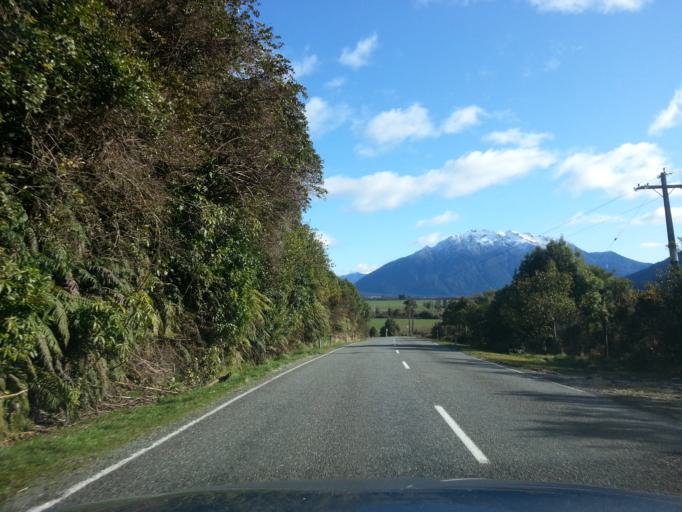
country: NZ
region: West Coast
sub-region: Grey District
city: Greymouth
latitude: -42.7413
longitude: 171.4263
